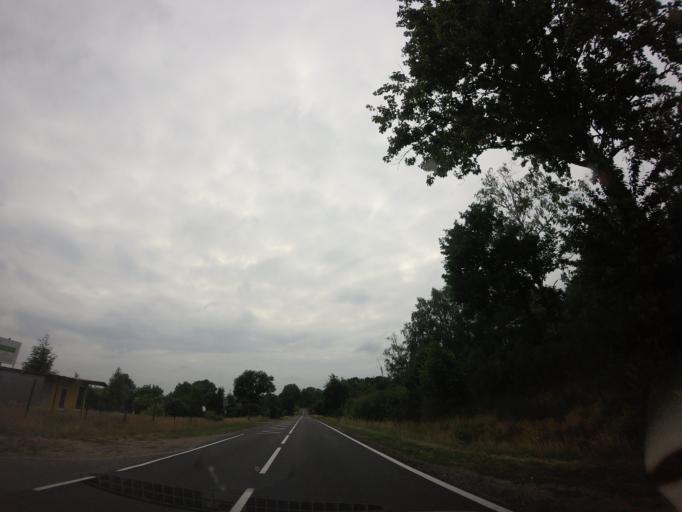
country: PL
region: West Pomeranian Voivodeship
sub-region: Powiat szczecinecki
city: Lubowo
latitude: 53.5905
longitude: 16.3607
